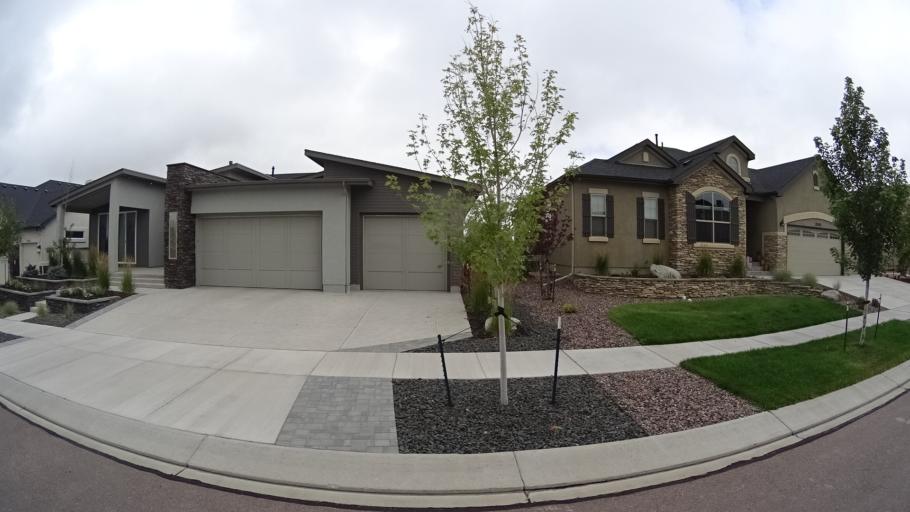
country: US
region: Colorado
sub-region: El Paso County
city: Gleneagle
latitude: 39.0106
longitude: -104.7870
